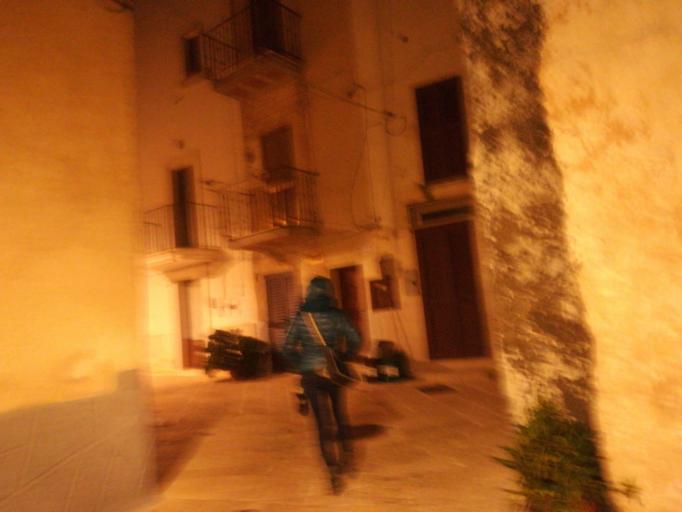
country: IT
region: Apulia
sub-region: Provincia di Bari
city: Monopoli
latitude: 40.9528
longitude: 17.3062
